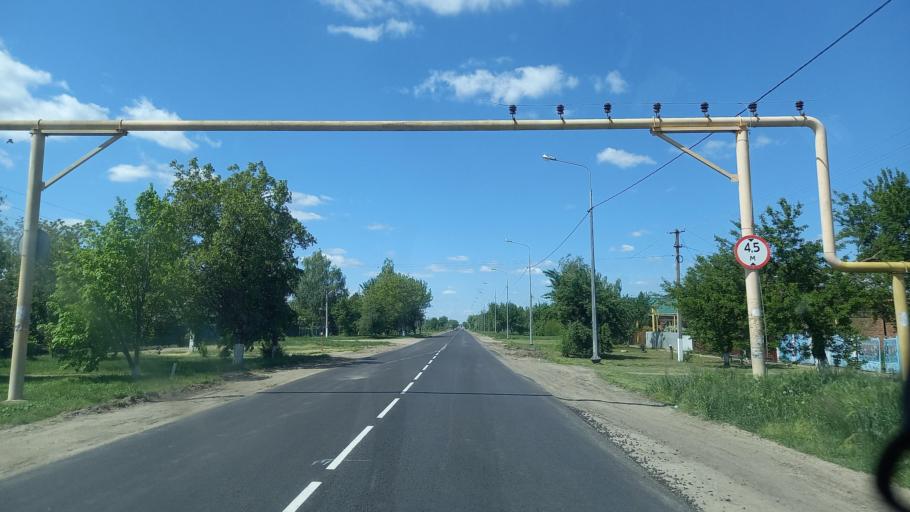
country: RU
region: Krasnodarskiy
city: Tbilisskaya
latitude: 45.3265
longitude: 40.2584
